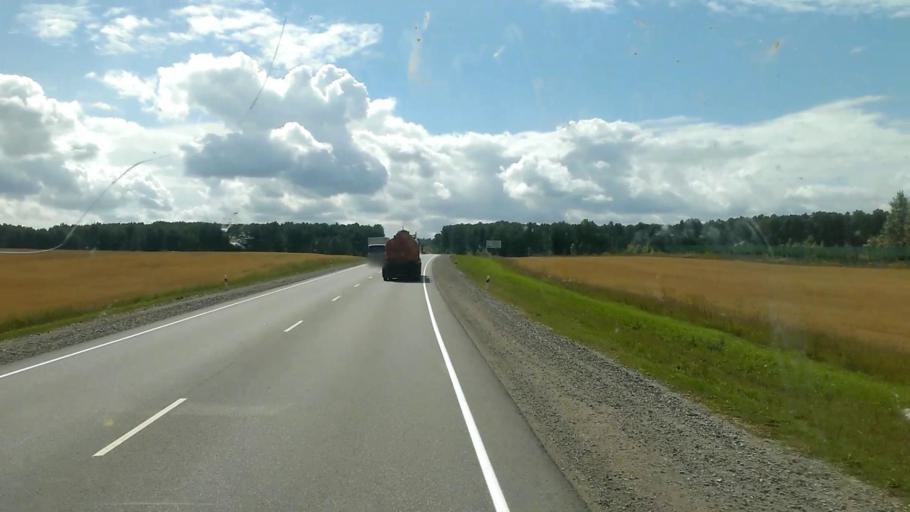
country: RU
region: Altai Krai
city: Troitskoye
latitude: 52.9875
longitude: 84.7434
